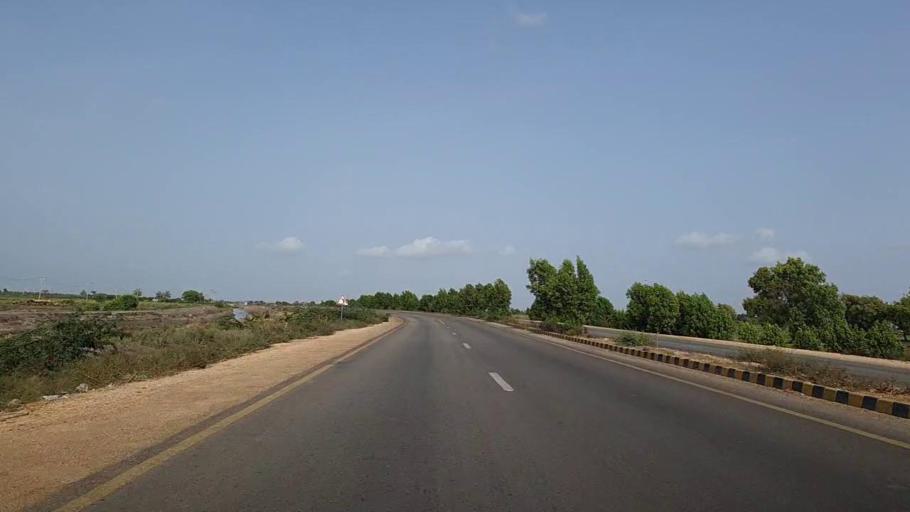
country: PK
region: Sindh
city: Thatta
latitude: 24.7425
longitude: 67.7981
